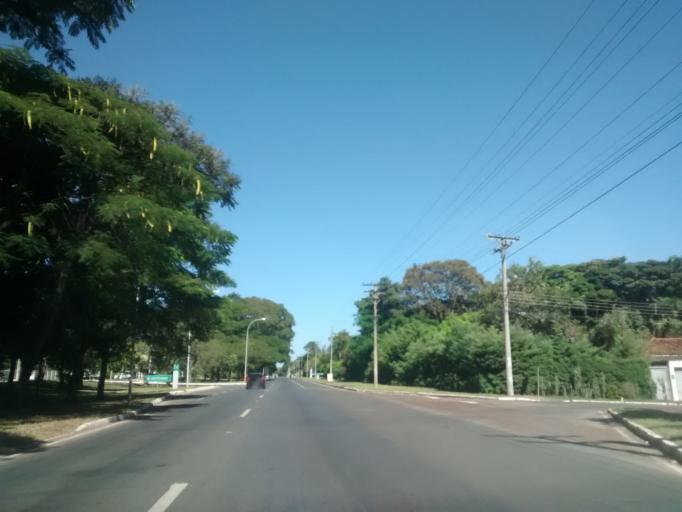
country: BR
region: Federal District
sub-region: Brasilia
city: Brasilia
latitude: -15.8470
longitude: -47.9008
